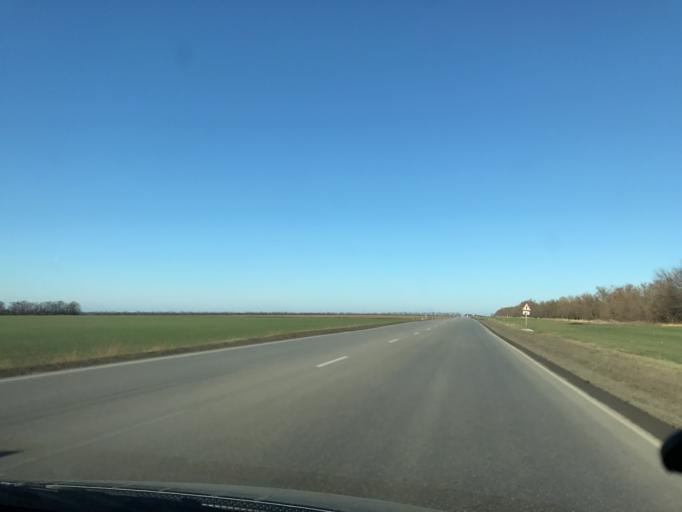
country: RU
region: Rostov
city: Kagal'nitskaya
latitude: 46.9147
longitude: 40.1102
